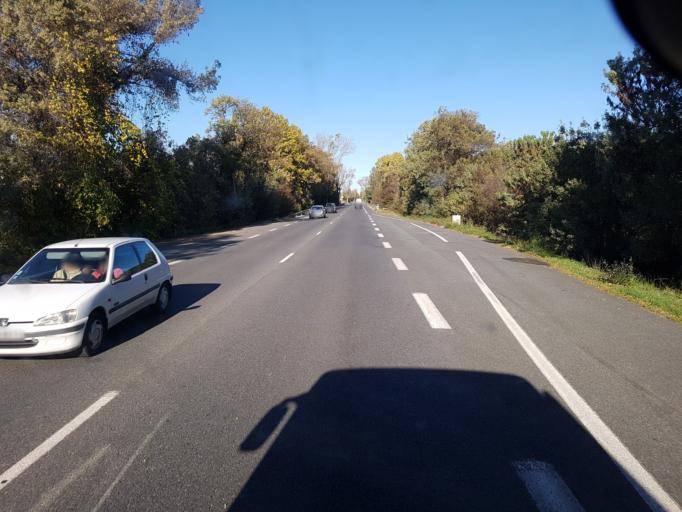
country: FR
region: Languedoc-Roussillon
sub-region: Departement de l'Aude
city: Narbonne
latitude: 43.2090
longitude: 3.0267
